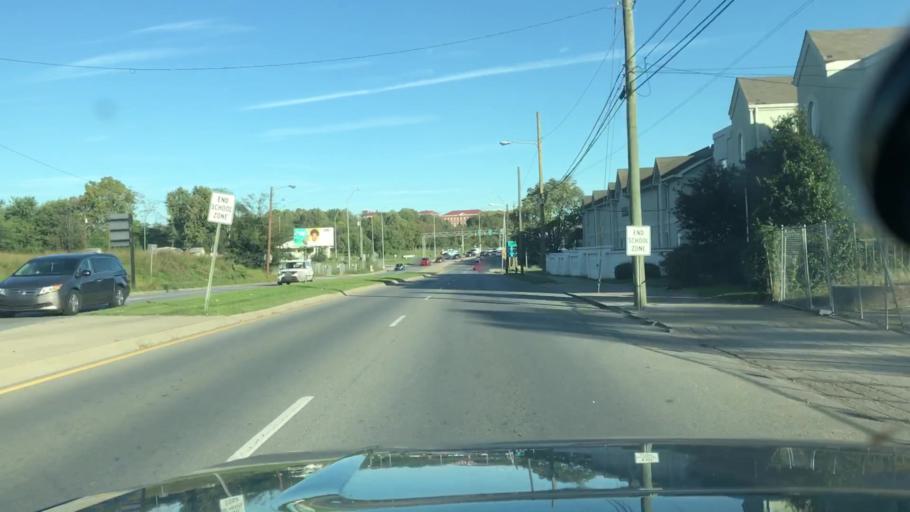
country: US
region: Tennessee
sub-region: Davidson County
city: Nashville
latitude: 36.1811
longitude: -86.7966
